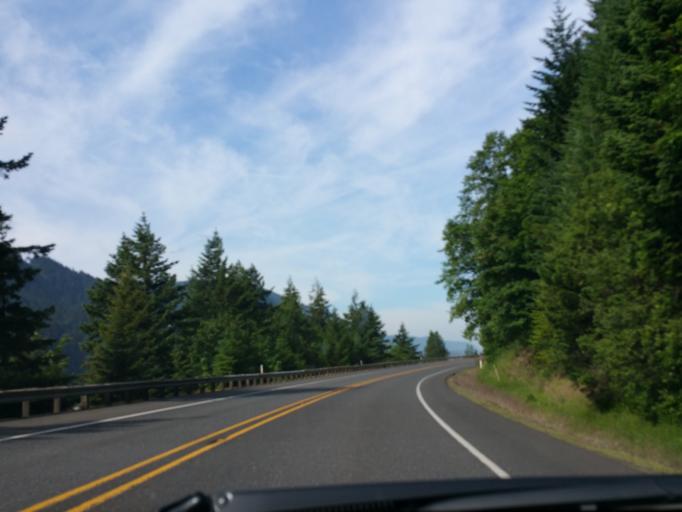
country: US
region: Oregon
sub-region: Hood River County
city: Cascade Locks
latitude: 45.6488
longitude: -121.9270
